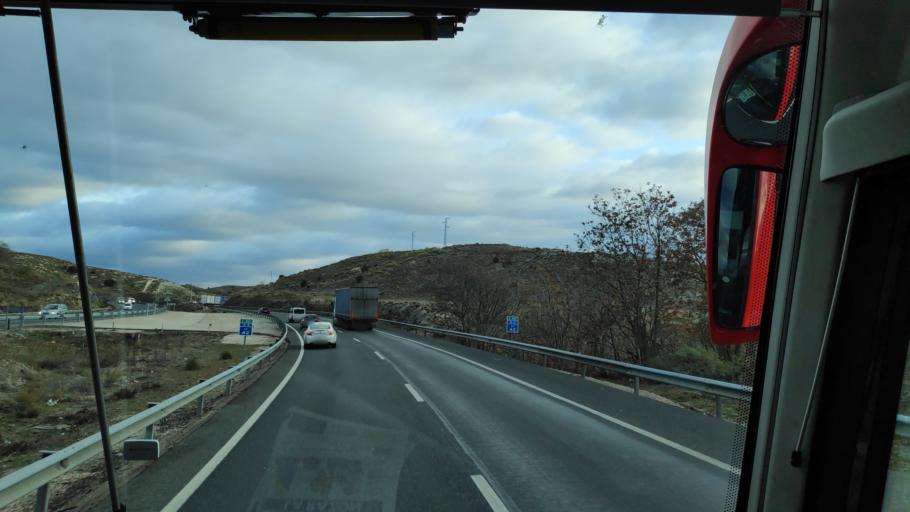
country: ES
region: Madrid
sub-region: Provincia de Madrid
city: Perales de Tajuna
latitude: 40.2153
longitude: -3.3290
